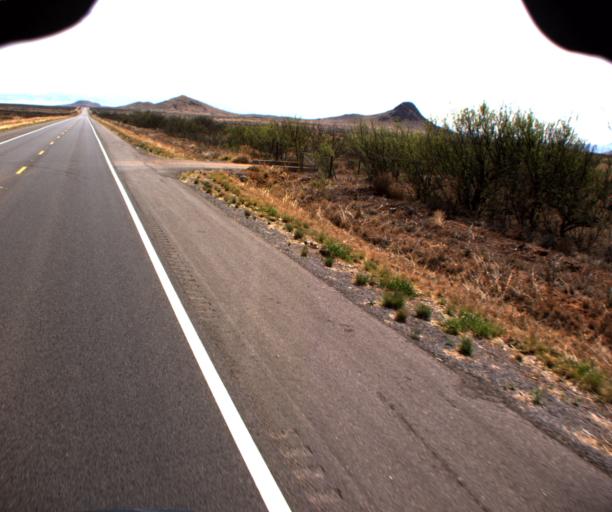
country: US
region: Arizona
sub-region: Cochise County
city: Tombstone
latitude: 31.9054
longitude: -109.7801
